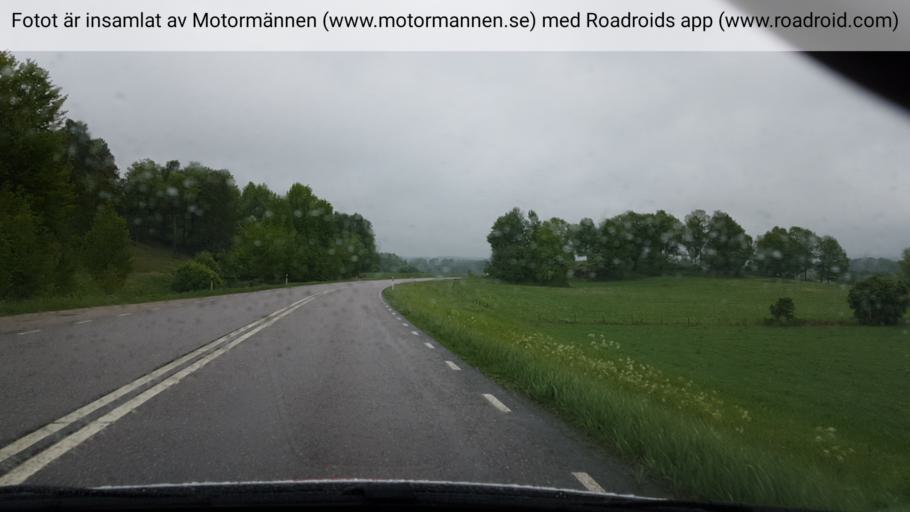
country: SE
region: Vaestra Goetaland
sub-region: Ulricehamns Kommun
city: Ulricehamn
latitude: 57.8876
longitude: 13.4352
